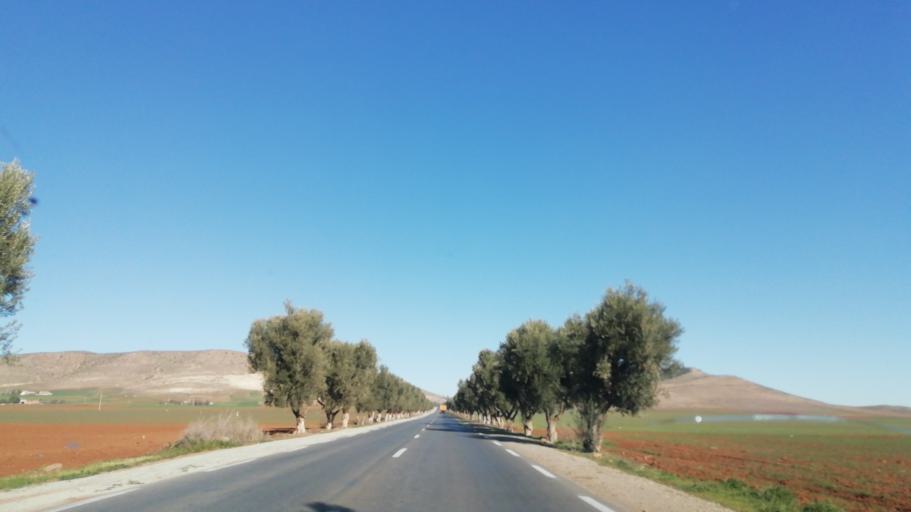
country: DZ
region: Mascara
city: Mascara
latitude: 35.2270
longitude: 0.1146
